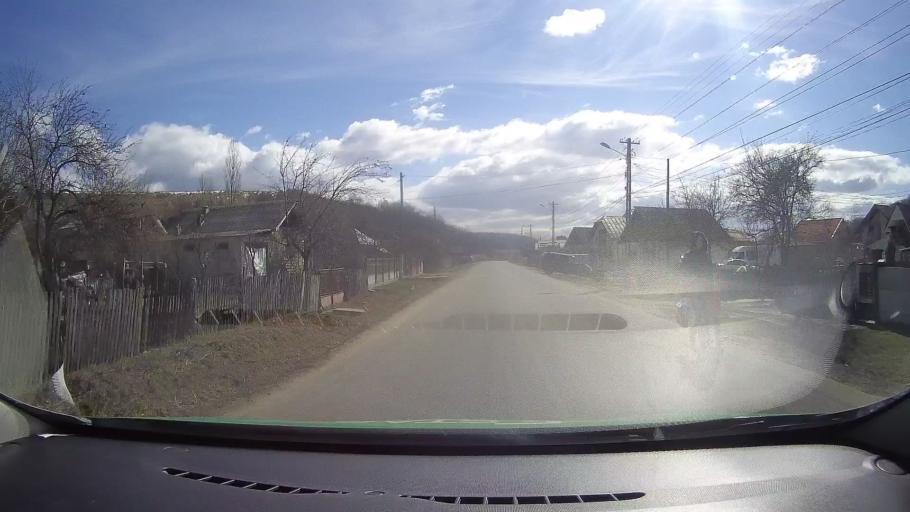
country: RO
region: Dambovita
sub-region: Comuna Vulcana-Pandele
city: Gura Vulcanei
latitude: 45.0356
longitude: 25.3919
